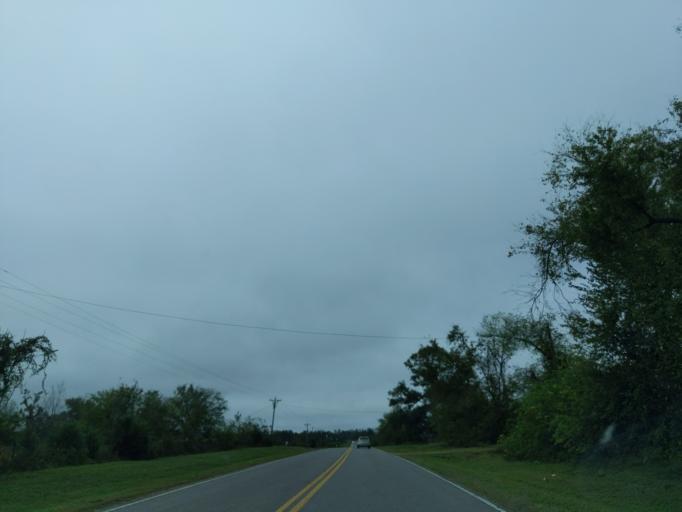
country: US
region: Florida
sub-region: Jackson County
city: Sneads
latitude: 30.6857
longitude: -84.9284
